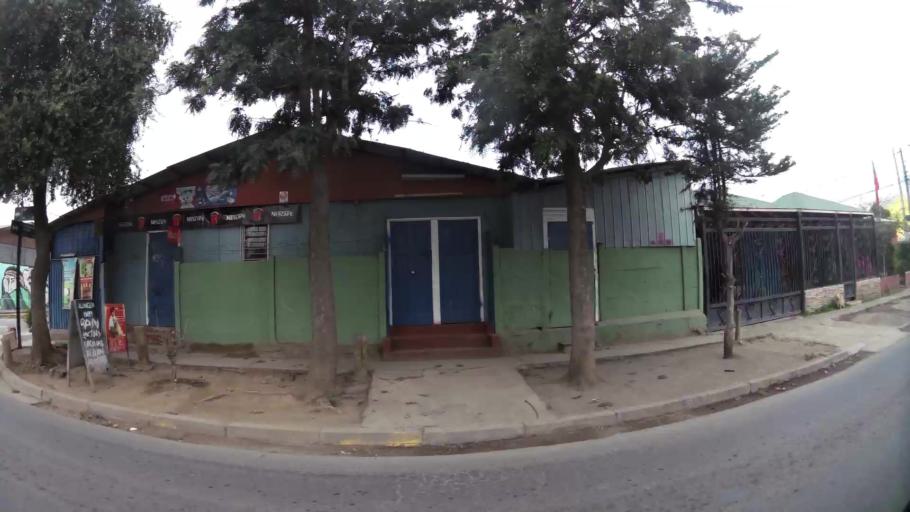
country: CL
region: Santiago Metropolitan
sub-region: Provincia de Chacabuco
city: Chicureo Abajo
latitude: -33.1925
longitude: -70.6744
